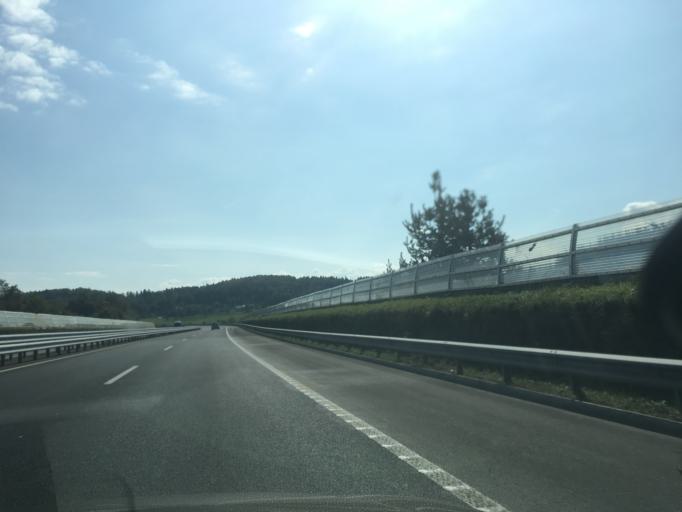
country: SI
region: Ivancna Gorica
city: Ivancna Gorica
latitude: 45.9419
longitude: 14.7805
